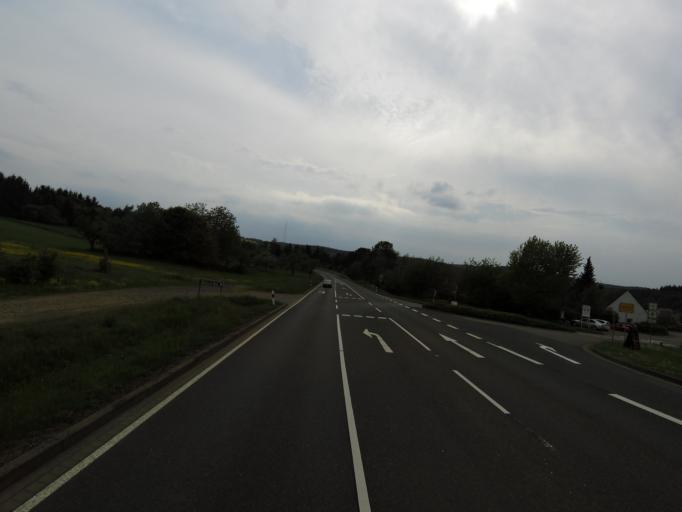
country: DE
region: Rheinland-Pfalz
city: Waldesch
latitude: 50.2873
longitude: 7.5491
